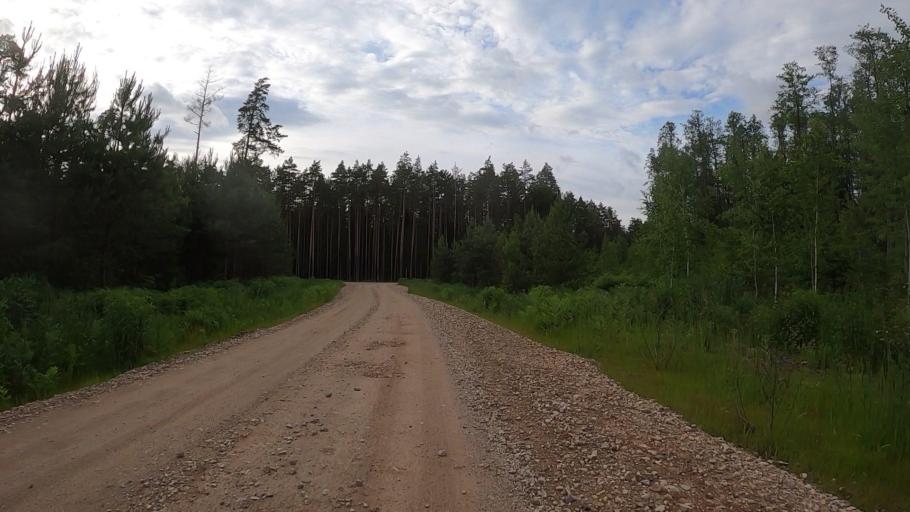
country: LV
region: Olaine
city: Olaine
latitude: 56.7697
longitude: 23.9036
